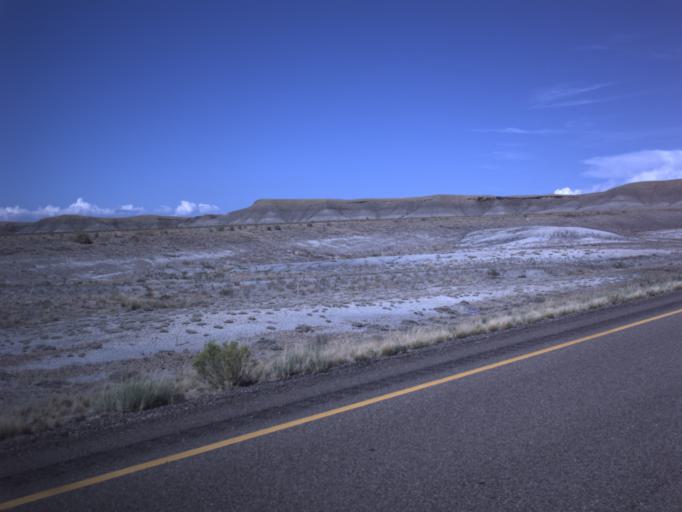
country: US
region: Utah
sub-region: Carbon County
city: East Carbon City
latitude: 38.9347
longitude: -110.3485
